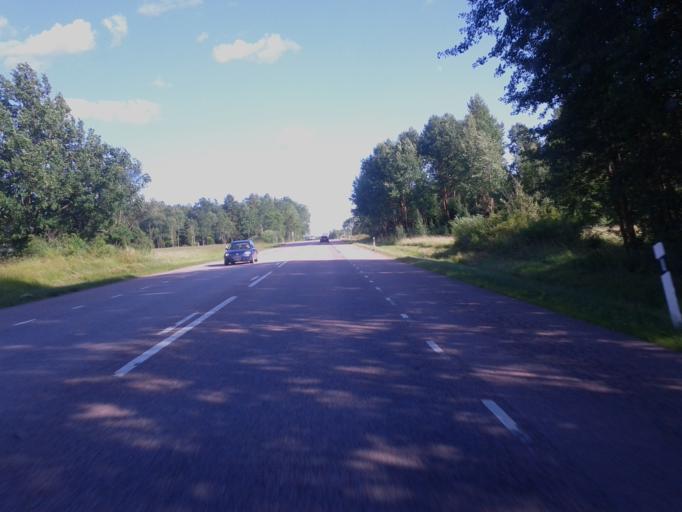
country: SE
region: Uppsala
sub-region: Enkopings Kommun
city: Enkoping
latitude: 59.6752
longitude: 17.0529
